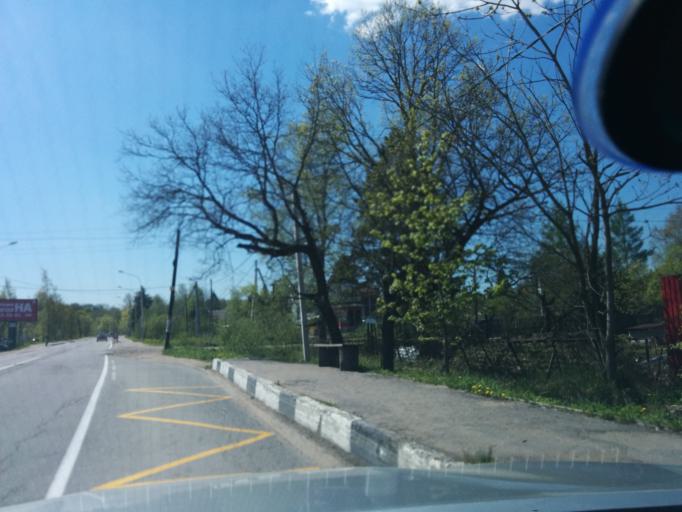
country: RU
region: Leningrad
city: Verkhniye Osel'ki
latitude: 60.2490
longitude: 30.4464
